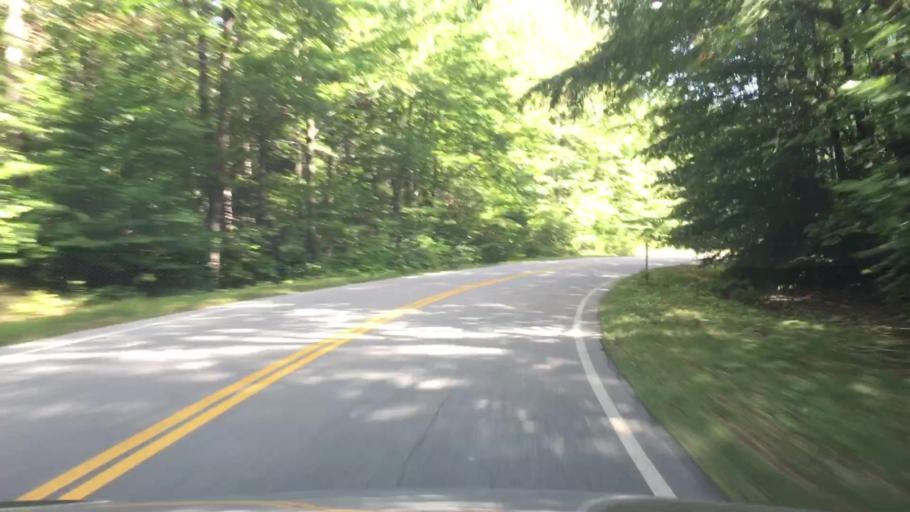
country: US
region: New Hampshire
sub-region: Carroll County
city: Tamworth
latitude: 44.0269
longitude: -71.3214
